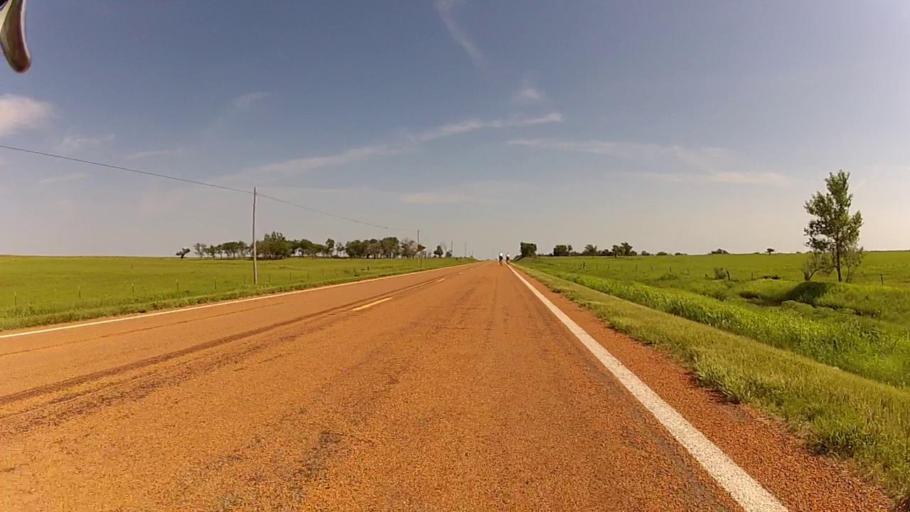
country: US
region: Kansas
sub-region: Cowley County
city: Winfield
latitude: 37.0804
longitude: -96.6436
